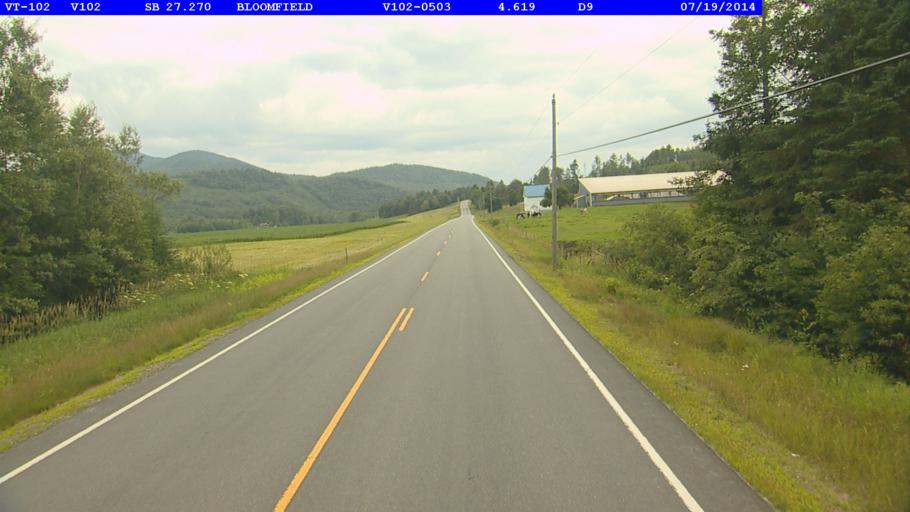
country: US
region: New Hampshire
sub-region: Coos County
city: Colebrook
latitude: 44.7975
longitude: -71.5758
